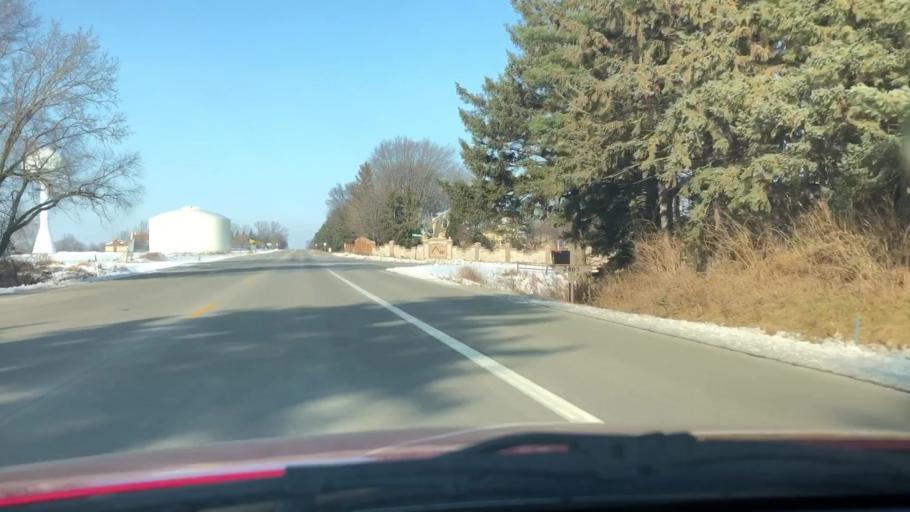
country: US
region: Wisconsin
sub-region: Outagamie County
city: Kimberly
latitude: 44.3326
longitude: -88.3750
